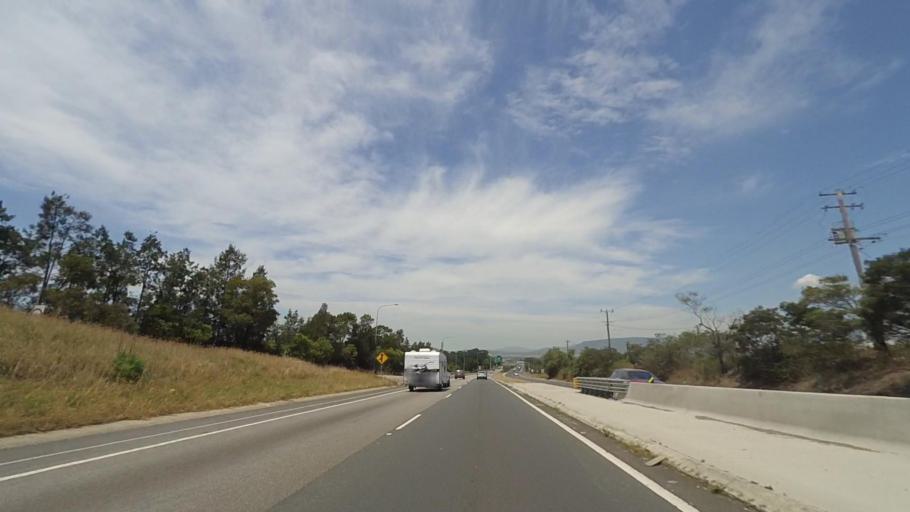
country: AU
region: New South Wales
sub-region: Shellharbour
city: Albion Park Rail
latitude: -34.5423
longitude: 150.7850
